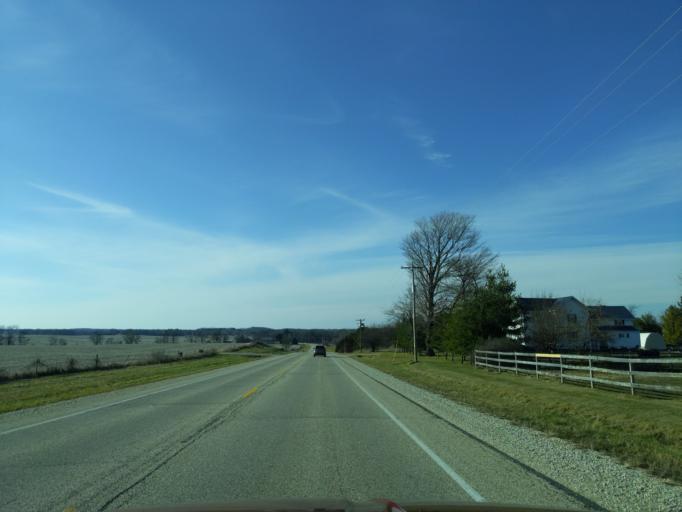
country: US
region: Wisconsin
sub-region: Rock County
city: Milton
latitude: 42.8298
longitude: -88.8622
